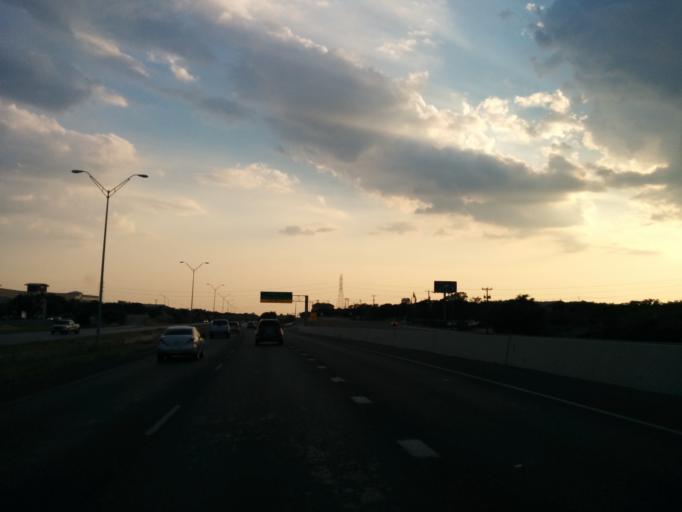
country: US
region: Texas
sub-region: Bexar County
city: Shavano Park
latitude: 29.6072
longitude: -98.5268
